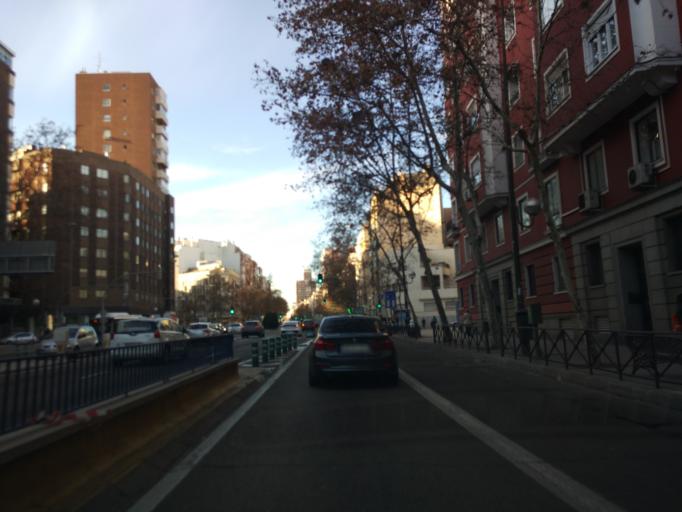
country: ES
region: Madrid
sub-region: Provincia de Madrid
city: Salamanca
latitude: 40.4312
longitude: -3.6713
